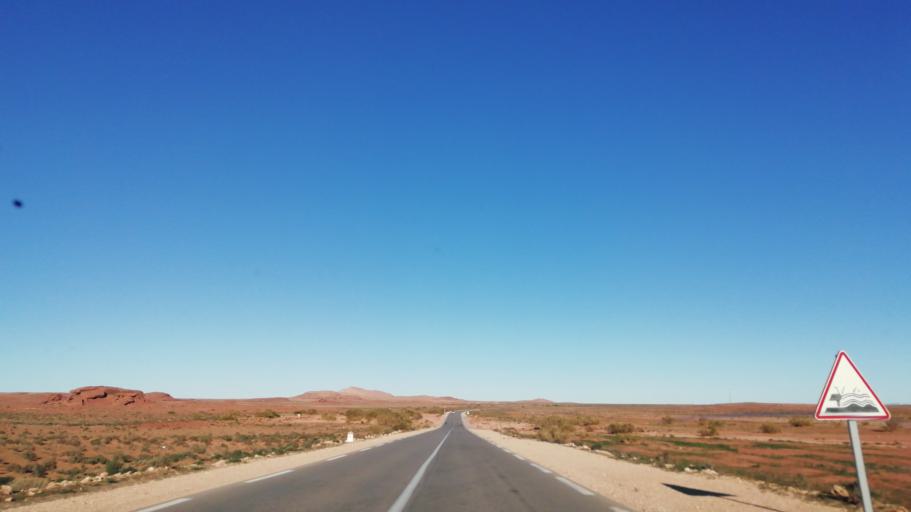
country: DZ
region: El Bayadh
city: El Abiodh Sidi Cheikh
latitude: 33.1067
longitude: 0.2176
